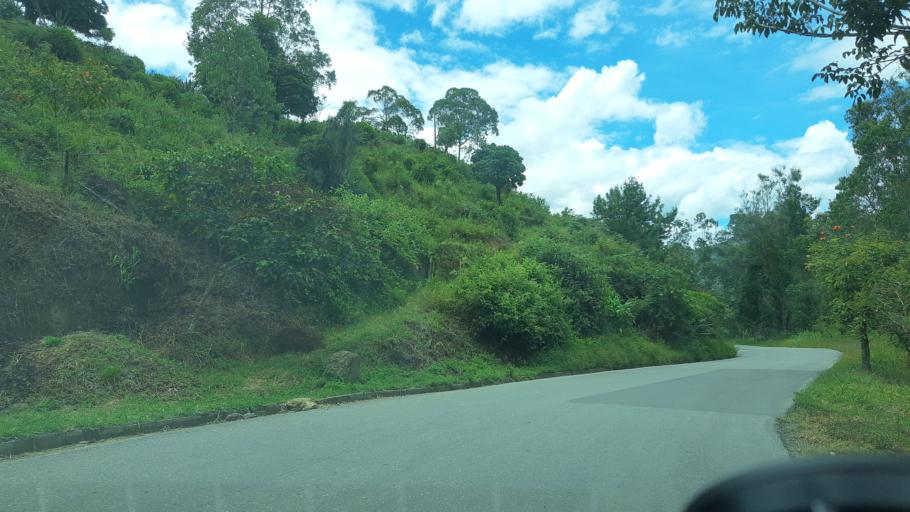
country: CO
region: Boyaca
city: Garagoa
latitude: 5.0499
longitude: -73.3871
